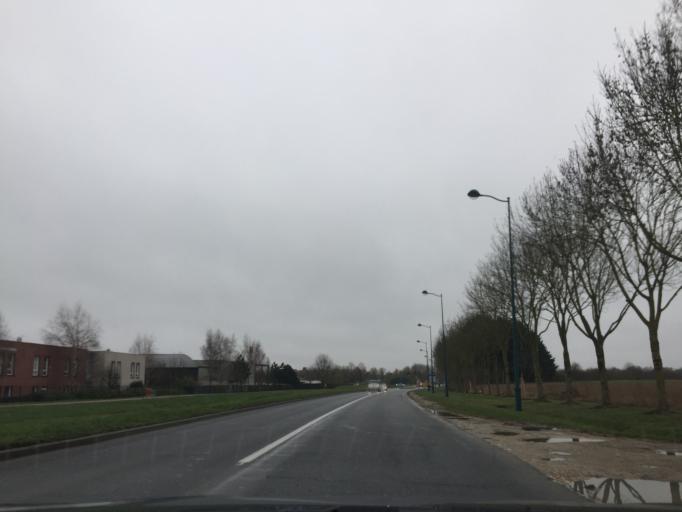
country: FR
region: Ile-de-France
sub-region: Departement de Seine-et-Marne
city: Magny-le-Hongre
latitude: 48.8644
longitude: 2.8076
